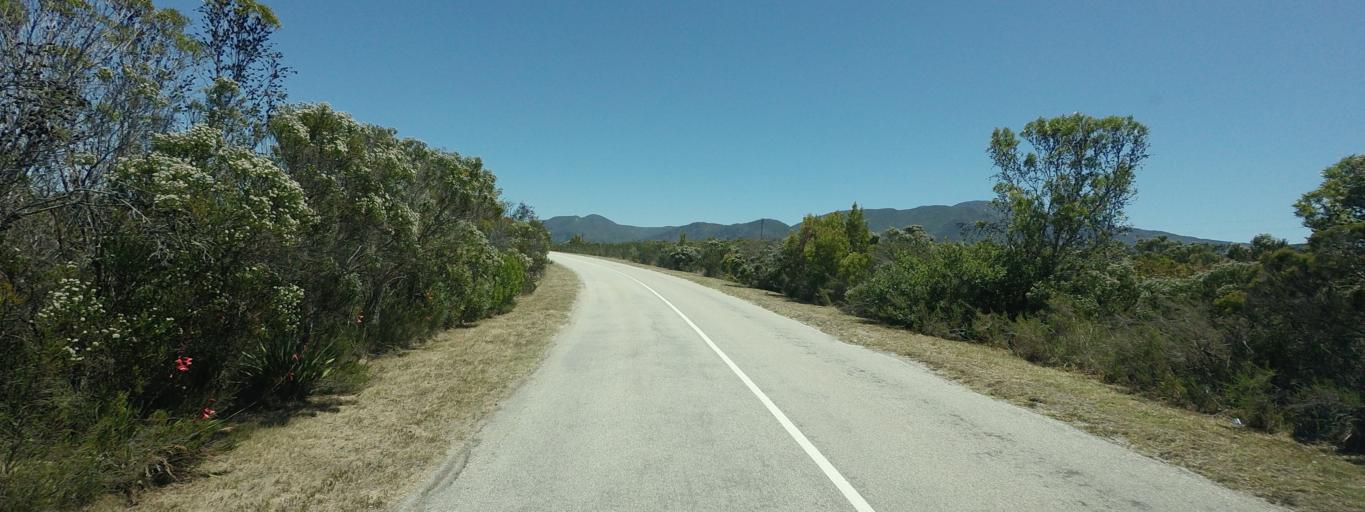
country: ZA
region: Western Cape
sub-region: Eden District Municipality
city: Plettenberg Bay
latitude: -33.9617
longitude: 23.5447
